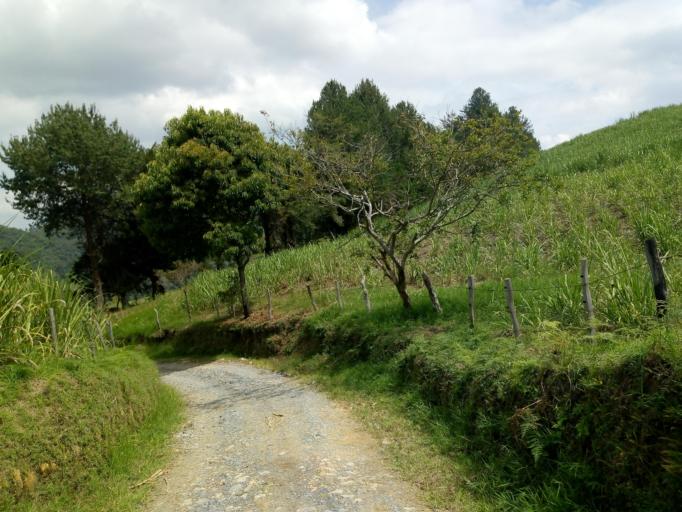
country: CO
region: Boyaca
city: Moniquira
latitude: 5.8650
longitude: -73.5274
